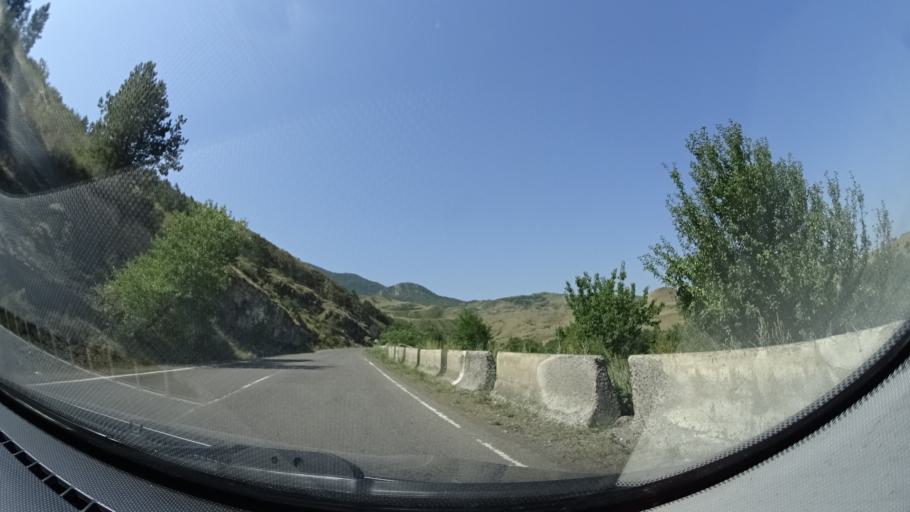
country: GE
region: Samtskhe-Javakheti
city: Aspindza
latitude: 41.6091
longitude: 43.1397
